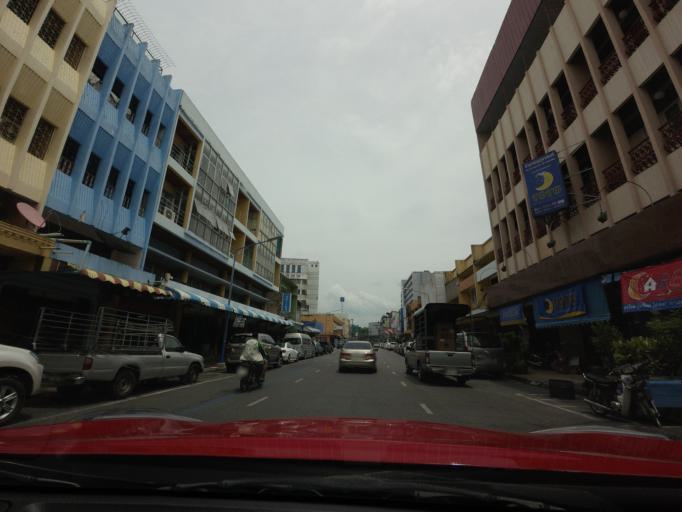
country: TH
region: Songkhla
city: Hat Yai
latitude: 6.9998
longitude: 100.4714
